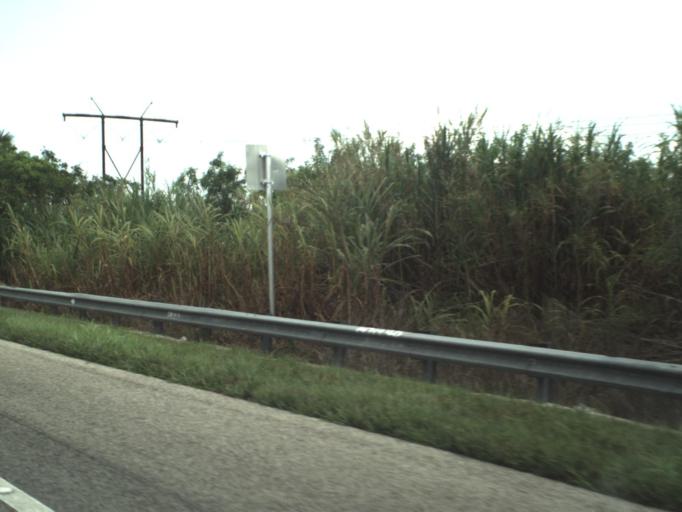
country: US
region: Florida
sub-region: Broward County
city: Weston
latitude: 26.3090
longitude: -80.5176
